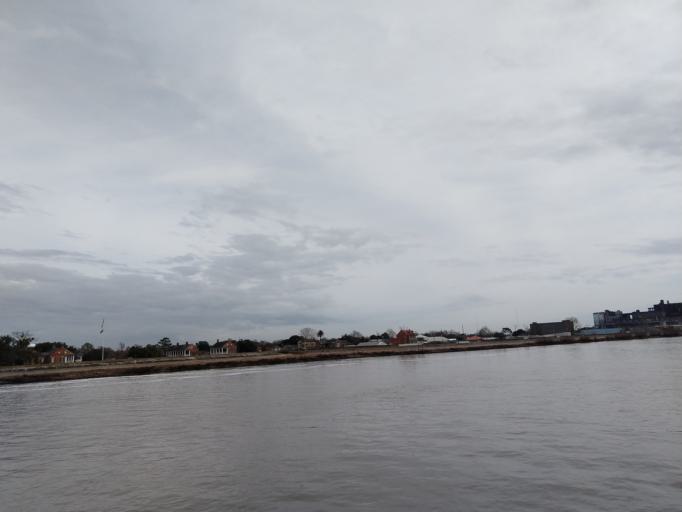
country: US
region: Louisiana
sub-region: Saint Bernard Parish
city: Arabi
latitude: 29.9483
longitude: -90.0128
